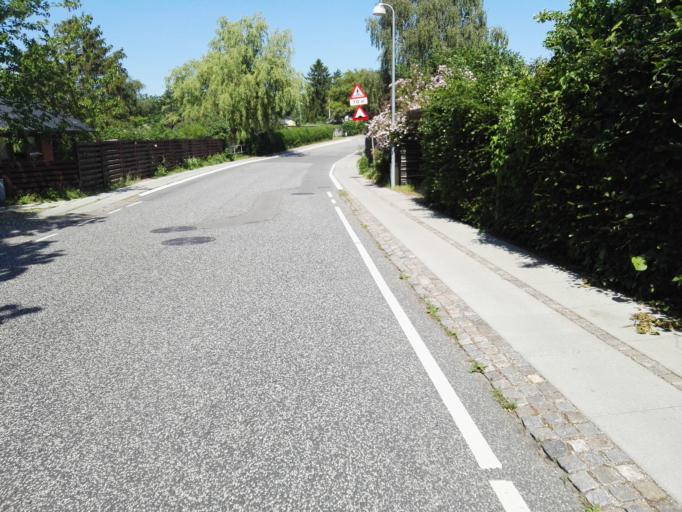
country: DK
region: Capital Region
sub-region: Fureso Kommune
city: Vaerlose
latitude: 55.7610
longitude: 12.3927
